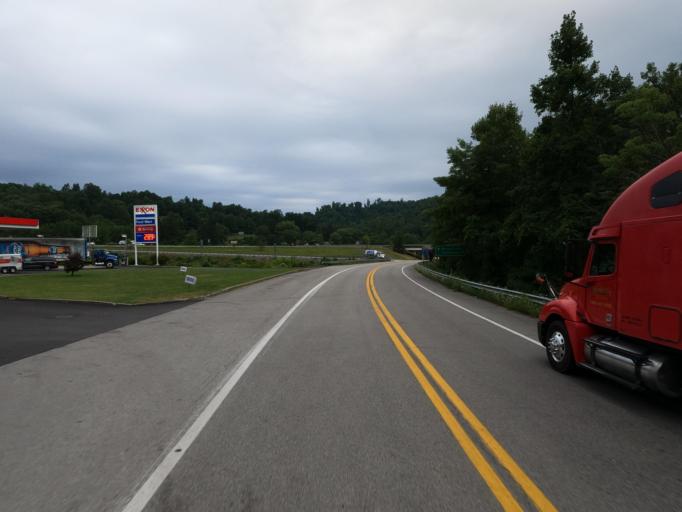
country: US
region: West Virginia
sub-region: Marion County
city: Fairmont
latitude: 39.4913
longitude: -80.0893
